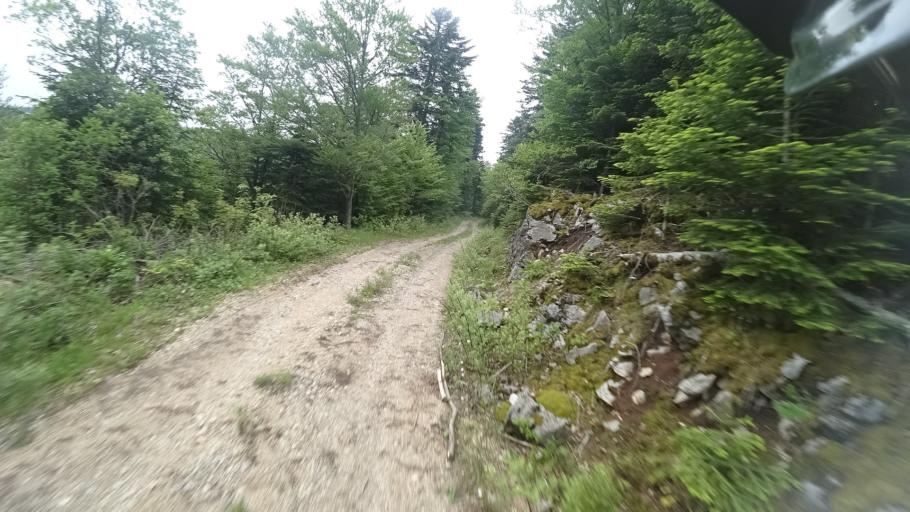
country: BA
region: Federation of Bosnia and Herzegovina
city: Bihac
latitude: 44.6282
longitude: 15.8039
